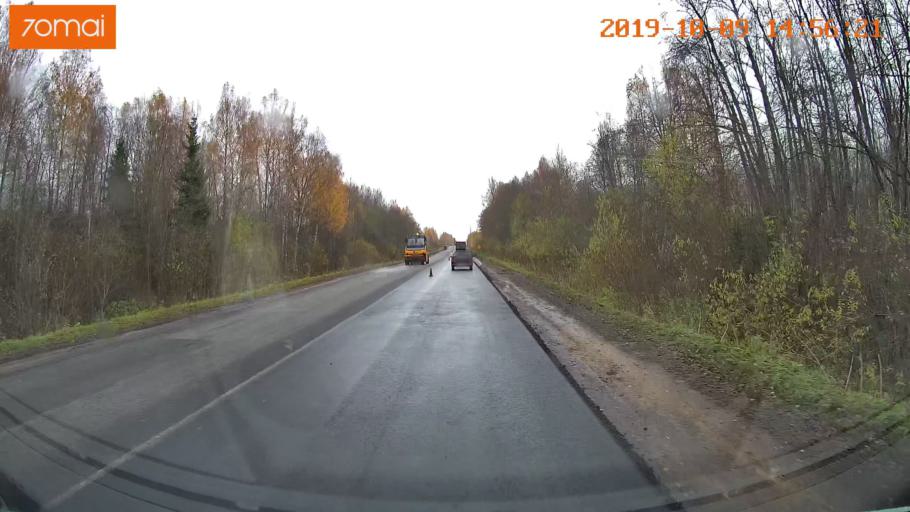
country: RU
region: Kostroma
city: Chistyye Bory
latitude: 58.3463
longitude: 41.6471
